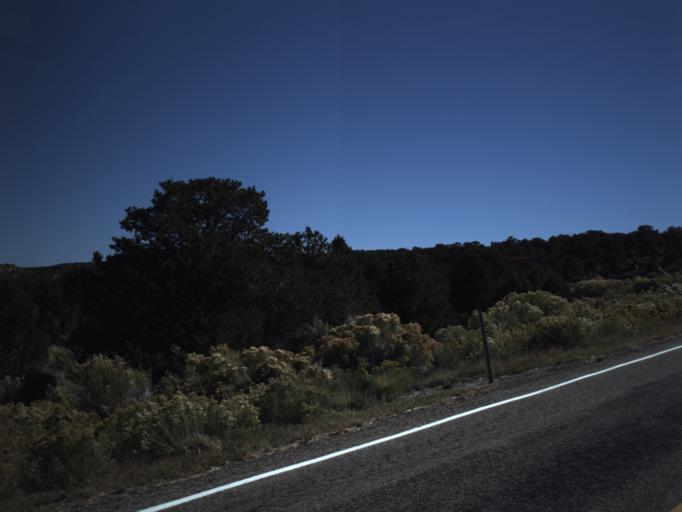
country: US
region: Utah
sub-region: Wayne County
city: Loa
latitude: 38.2321
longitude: -111.3621
